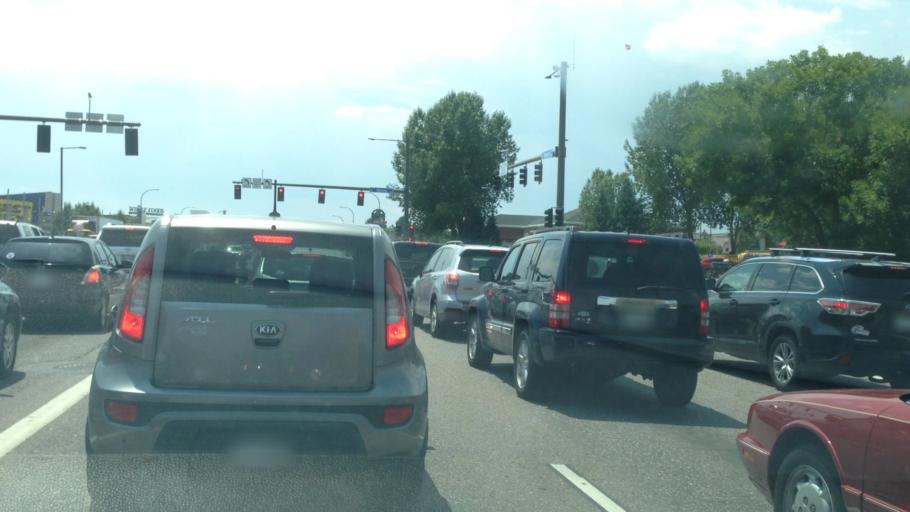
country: US
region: Colorado
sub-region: Jefferson County
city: Lakewood
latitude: 39.7116
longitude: -105.0816
